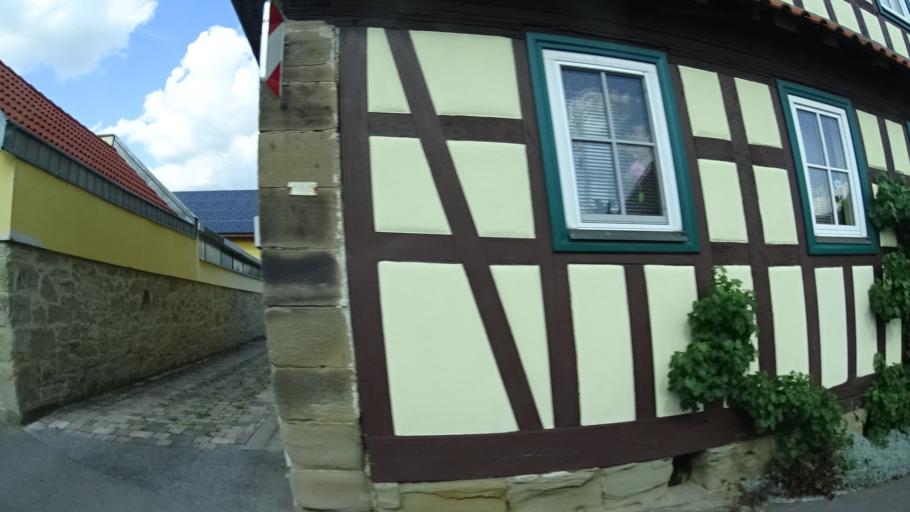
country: DE
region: Bavaria
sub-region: Regierungsbezirk Unterfranken
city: Bundorf
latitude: 50.2744
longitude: 10.5239
